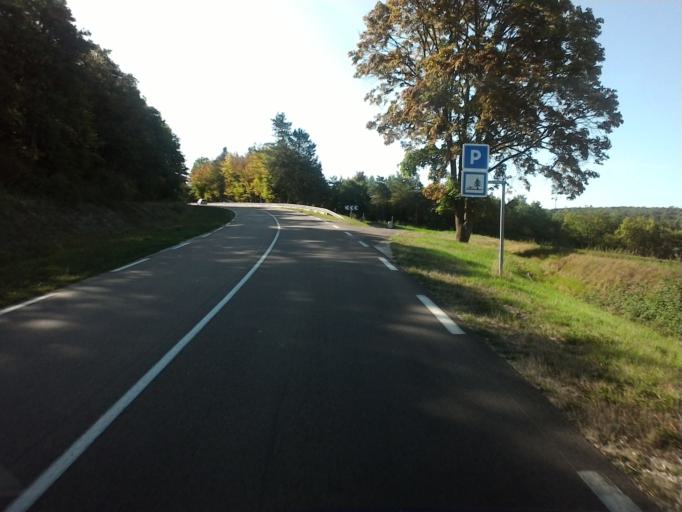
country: FR
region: Champagne-Ardenne
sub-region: Departement de l'Aube
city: Mussy-sur-Seine
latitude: 48.0022
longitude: 4.4744
